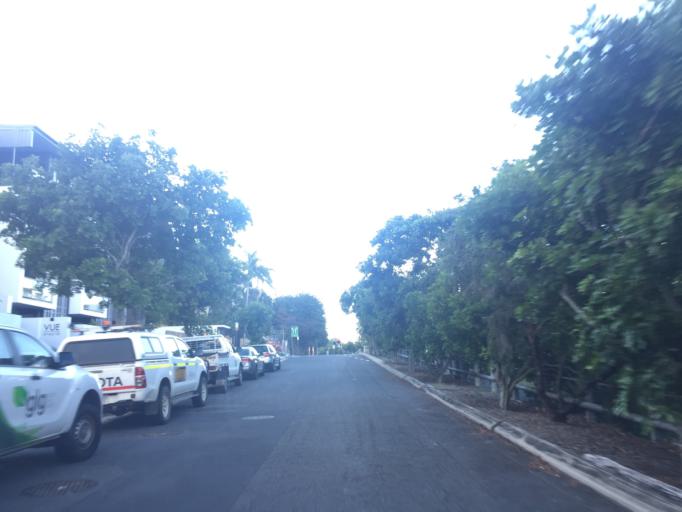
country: AU
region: Queensland
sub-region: Brisbane
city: Spring Hill
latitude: -27.4572
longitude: 153.0126
